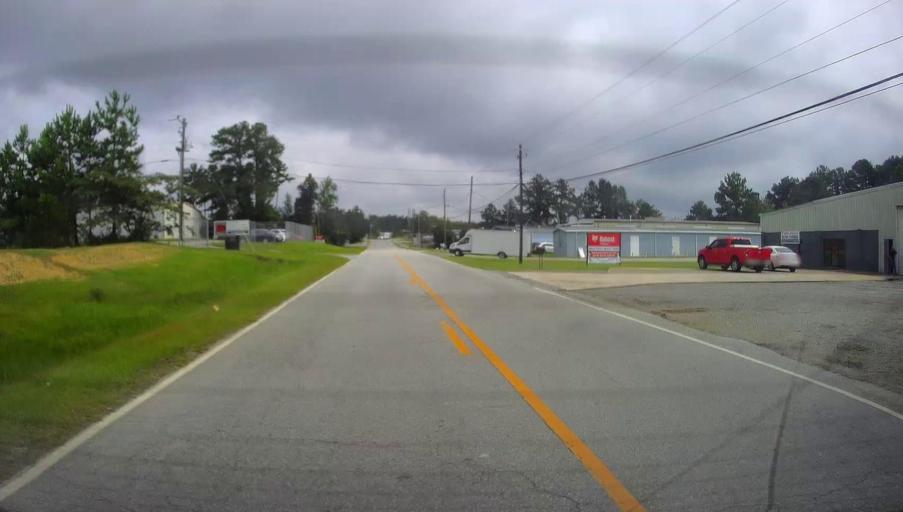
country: US
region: Georgia
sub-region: Bibb County
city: West Point
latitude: 32.8298
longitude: -83.7292
